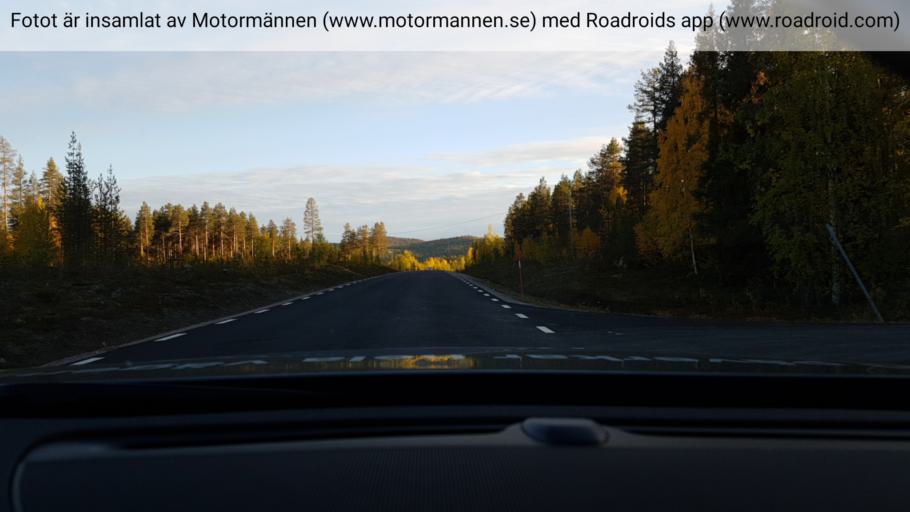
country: SE
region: Norrbotten
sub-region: Jokkmokks Kommun
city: Jokkmokk
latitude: 66.5810
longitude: 19.8050
